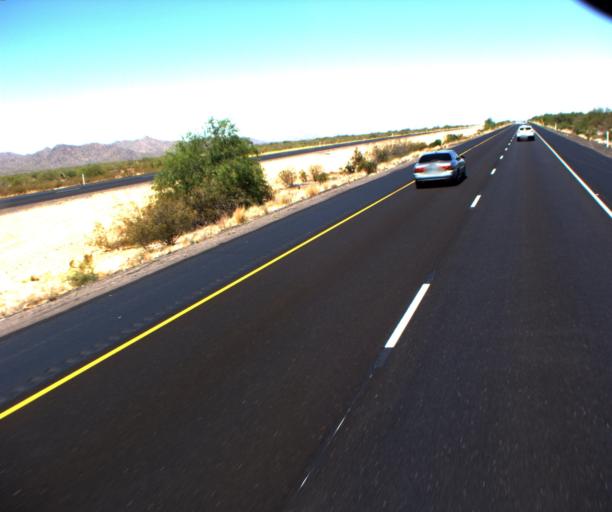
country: US
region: Arizona
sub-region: Yavapai County
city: Congress
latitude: 34.0817
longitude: -112.8906
